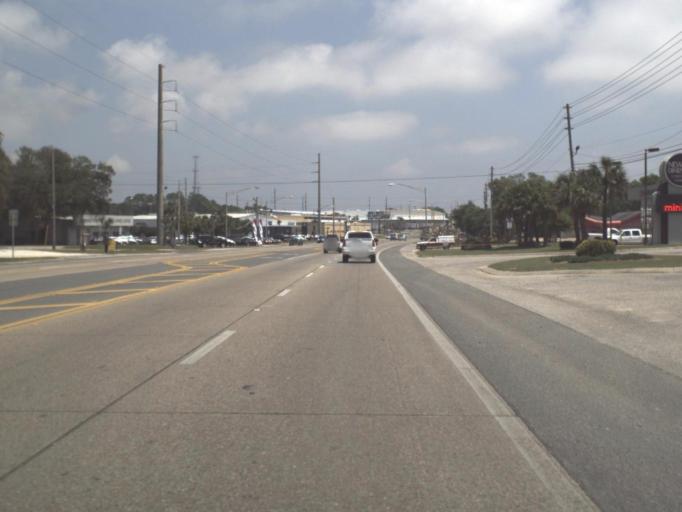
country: US
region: Florida
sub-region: Escambia County
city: West Pensacola
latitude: 30.4118
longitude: -87.2542
